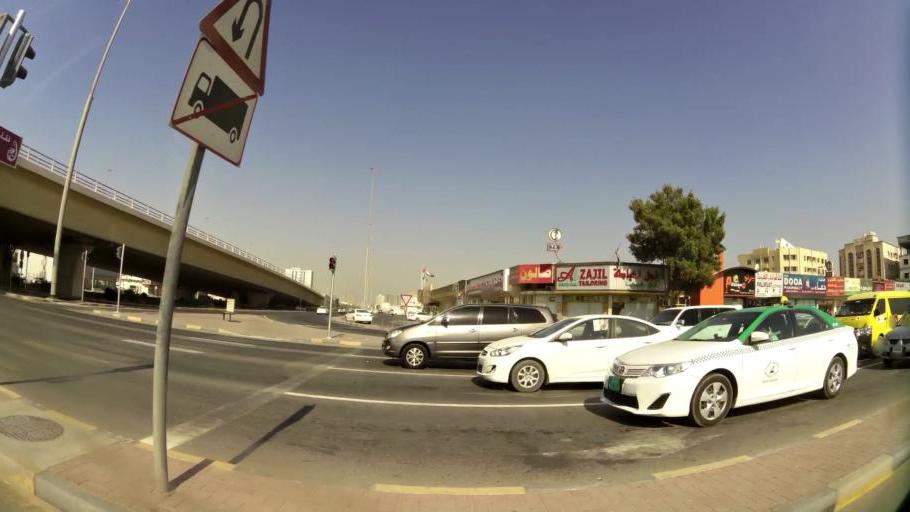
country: AE
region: Ajman
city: Ajman
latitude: 25.3990
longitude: 55.5047
